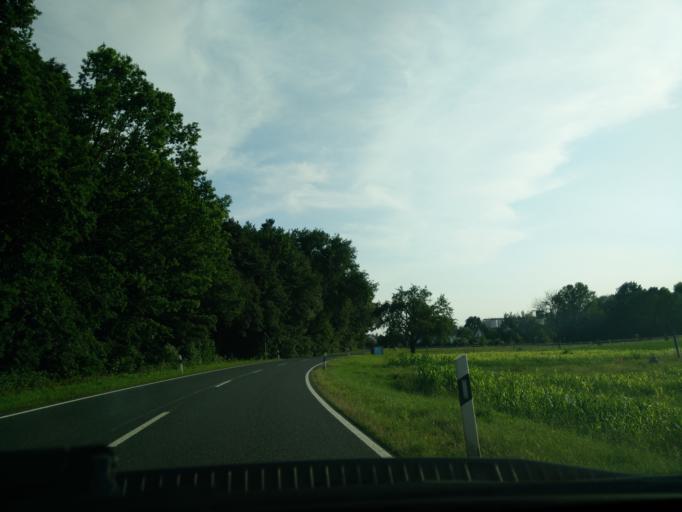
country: DE
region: Saxony
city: Frohburg
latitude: 51.0738
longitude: 12.5605
